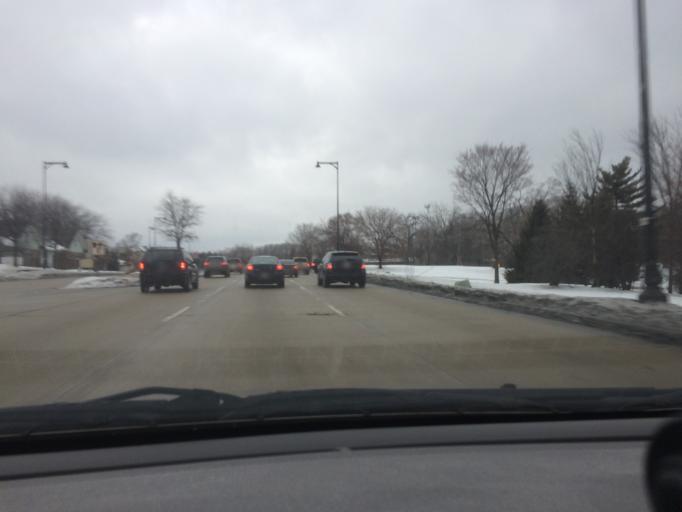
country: US
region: Illinois
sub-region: DuPage County
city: Bloomingdale
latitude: 41.9580
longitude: -88.0837
